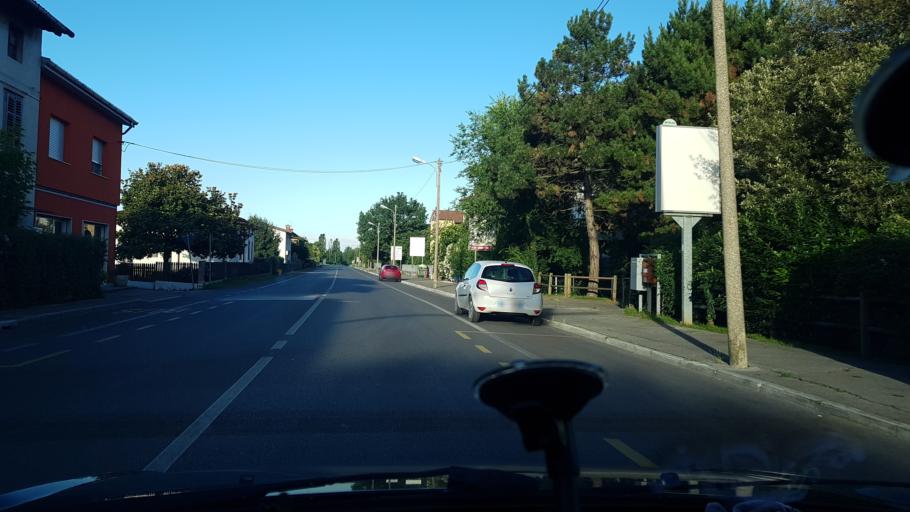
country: IT
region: Friuli Venezia Giulia
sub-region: Provincia di Gorizia
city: Savogna d'Isonzo
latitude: 45.9350
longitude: 13.5914
